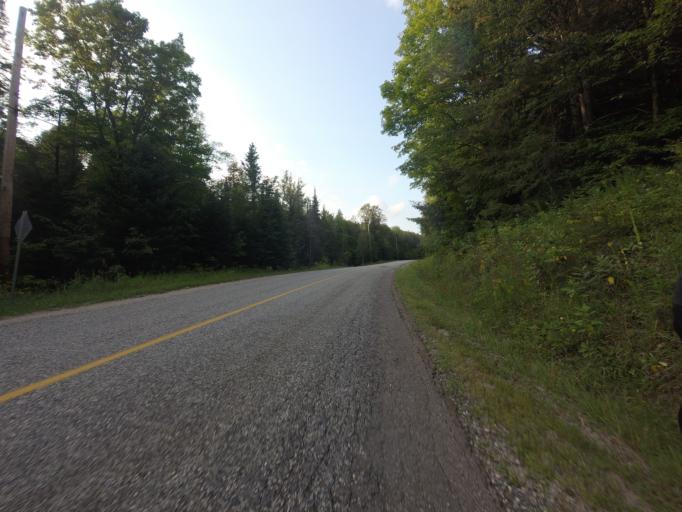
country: CA
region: Ontario
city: Renfrew
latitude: 44.9807
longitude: -76.7409
